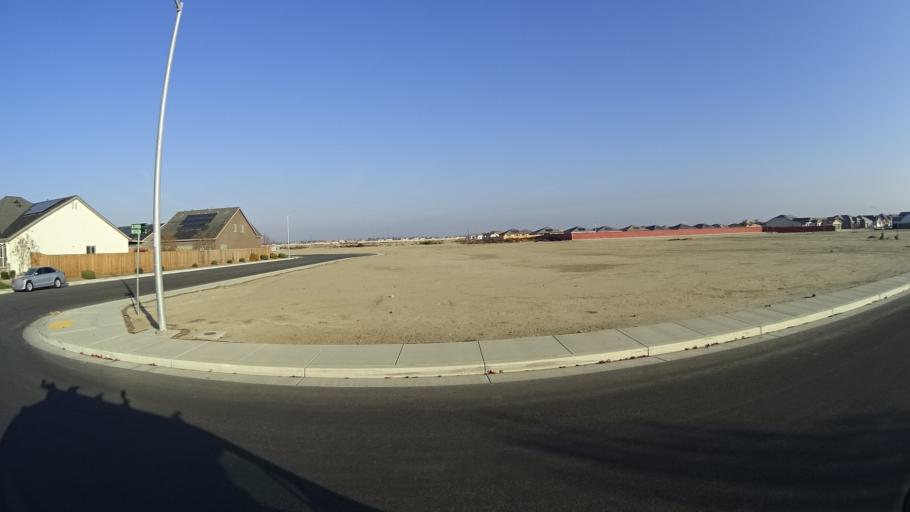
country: US
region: California
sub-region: Kern County
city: Greenacres
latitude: 35.2911
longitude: -119.1148
